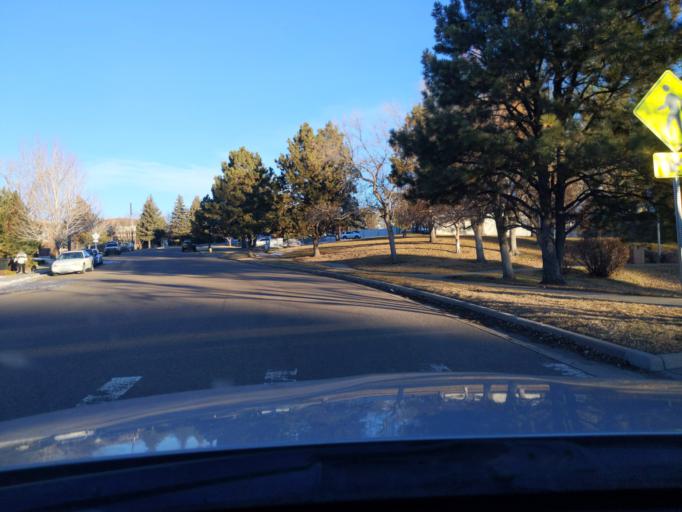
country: US
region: Colorado
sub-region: Arapahoe County
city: Centennial
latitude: 39.5699
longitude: -104.8829
